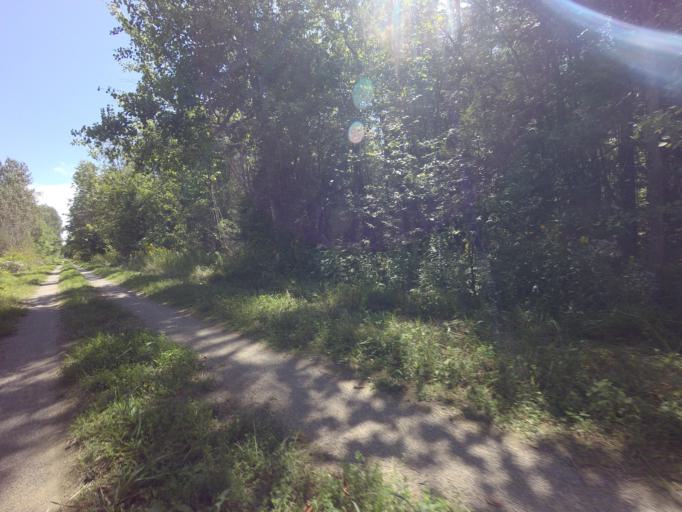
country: CA
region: Ontario
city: Orangeville
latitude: 43.7761
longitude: -80.2009
